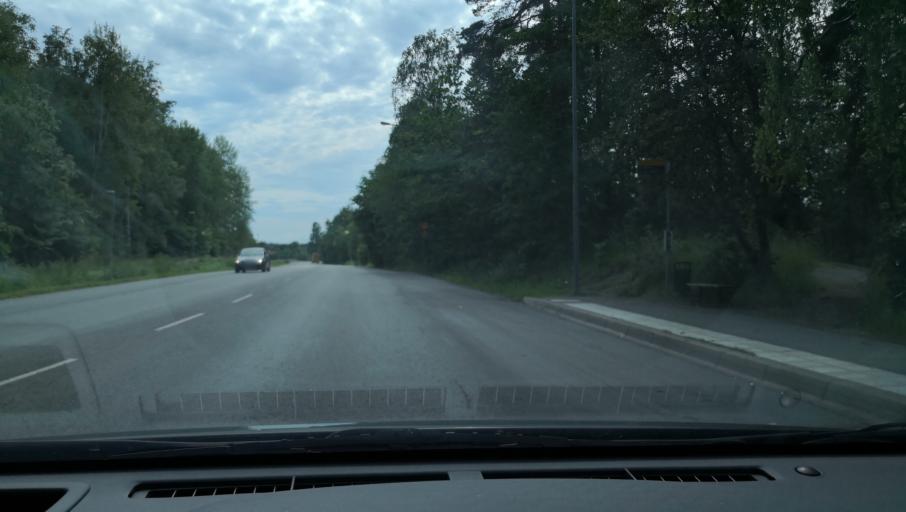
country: SE
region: Uppsala
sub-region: Uppsala Kommun
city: Uppsala
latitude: 59.8264
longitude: 17.6293
